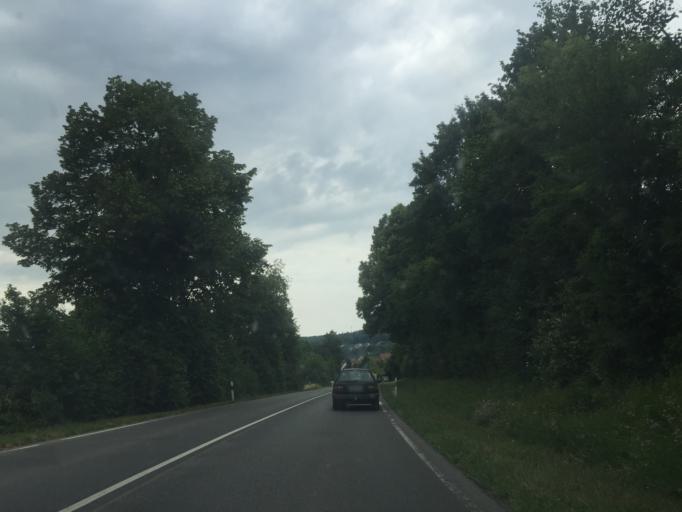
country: DE
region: Baden-Wuerttemberg
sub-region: Karlsruhe Region
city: Zuzenhausen
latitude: 49.2664
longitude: 8.8434
